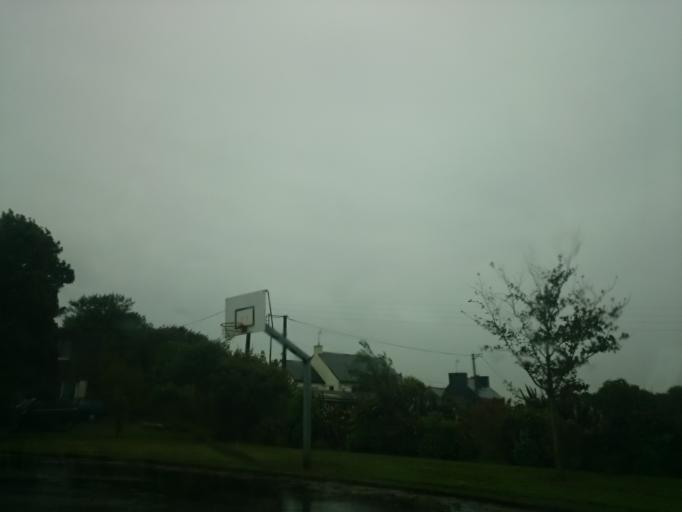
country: FR
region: Brittany
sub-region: Departement du Finistere
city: Kernilis
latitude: 48.5546
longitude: -4.4048
